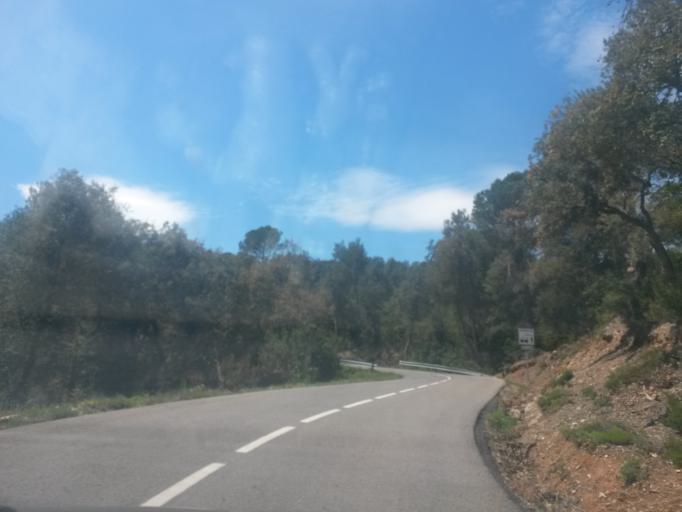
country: ES
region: Catalonia
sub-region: Provincia de Girona
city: Madremanya
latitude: 41.9389
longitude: 2.9463
